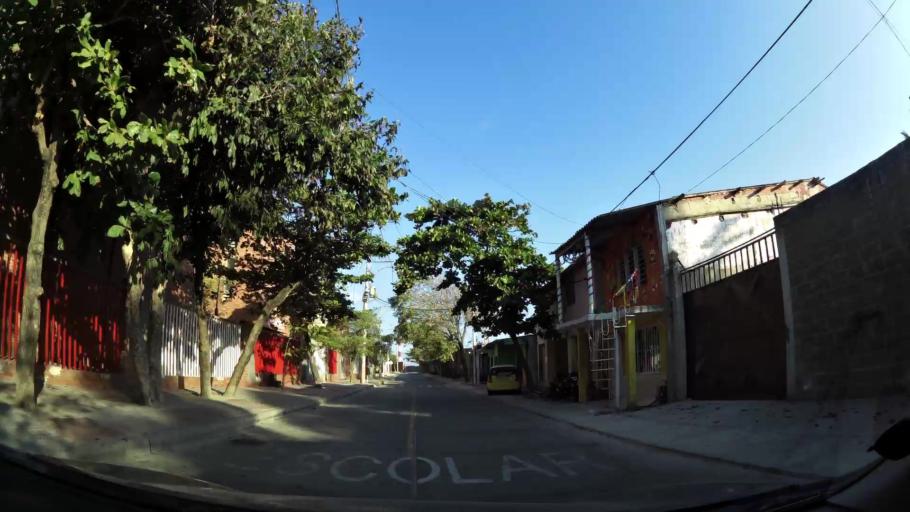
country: CO
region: Atlantico
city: Barranquilla
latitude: 11.0414
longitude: -74.8248
